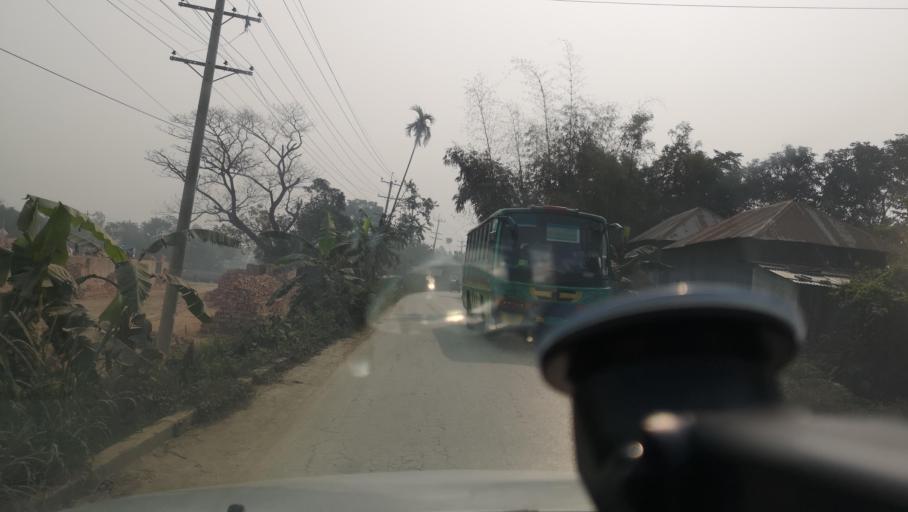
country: BD
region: Dhaka
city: Mirzapur
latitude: 23.9532
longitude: 90.0974
